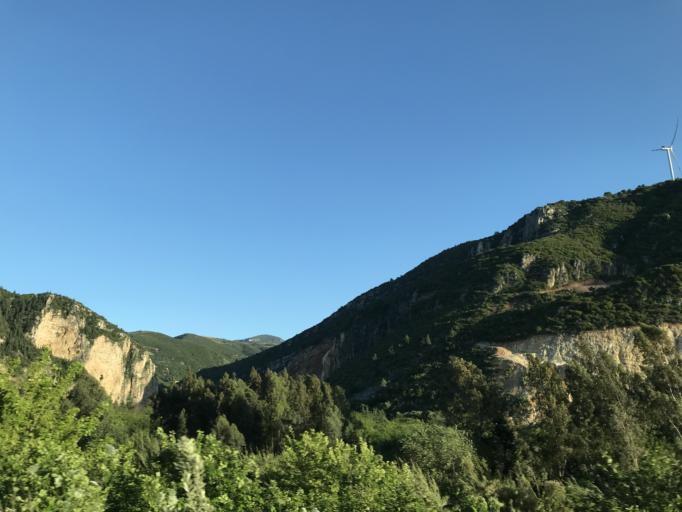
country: TR
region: Hatay
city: Samandag
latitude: 36.0764
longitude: 36.0259
